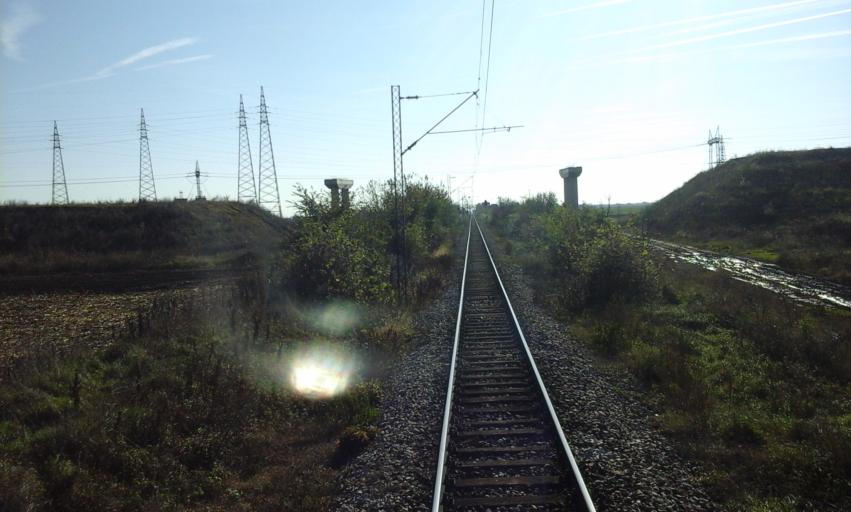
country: RS
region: Autonomna Pokrajina Vojvodina
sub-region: Severnobacki Okrug
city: Subotica
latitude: 46.0348
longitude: 19.6829
